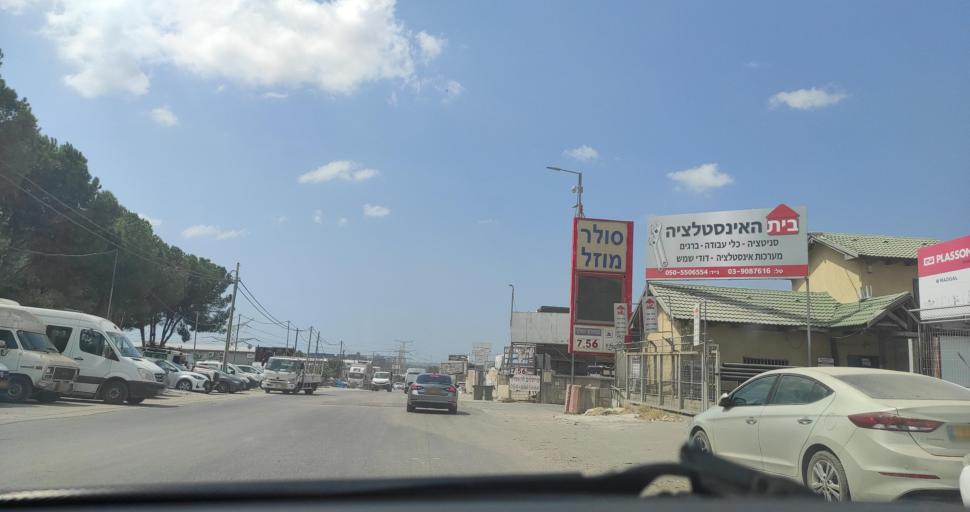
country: IL
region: Central District
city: Kafr Qasim
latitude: 32.1129
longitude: 34.9598
